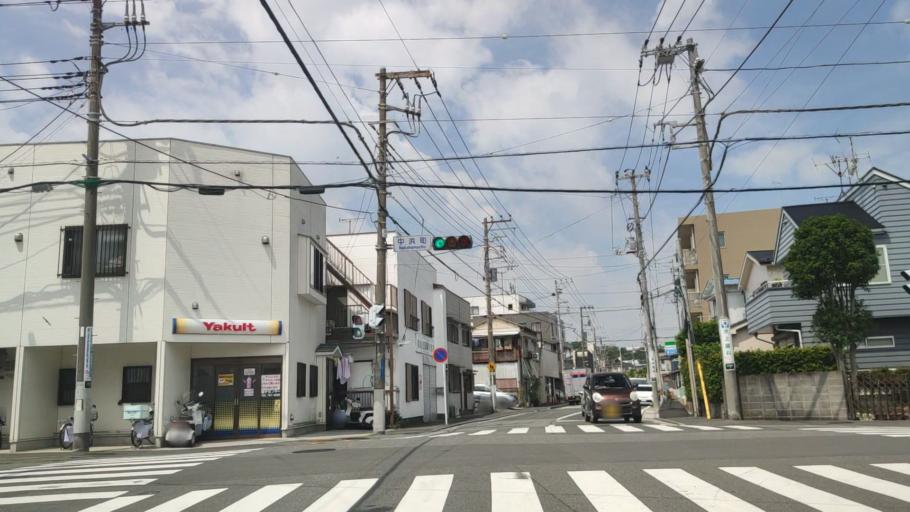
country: JP
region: Kanagawa
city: Yokohama
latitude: 35.4167
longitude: 139.6238
